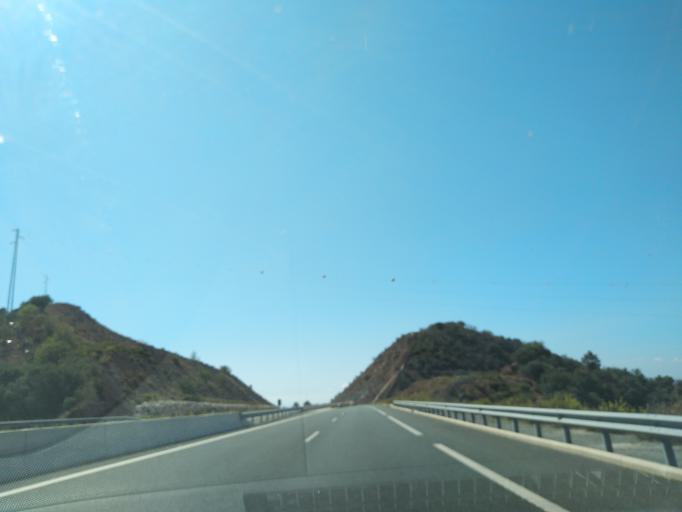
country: ES
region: Andalusia
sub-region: Provincia de Malaga
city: Almogia
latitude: 36.8246
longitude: -4.4700
